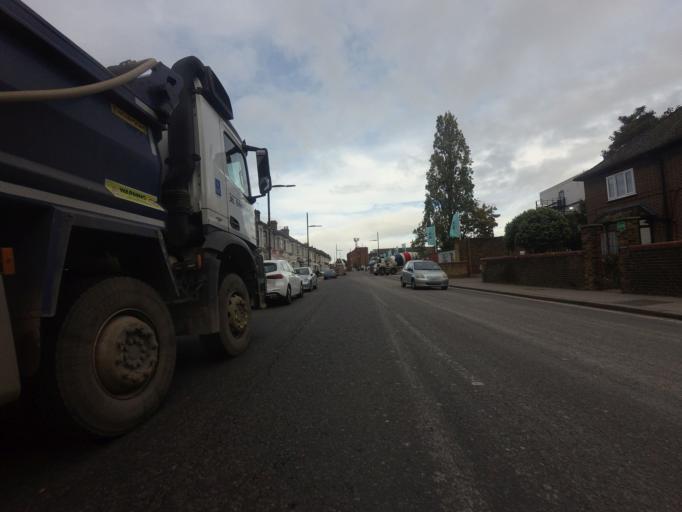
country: GB
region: England
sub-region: Greater London
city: East Ham
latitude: 51.5311
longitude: 0.0376
